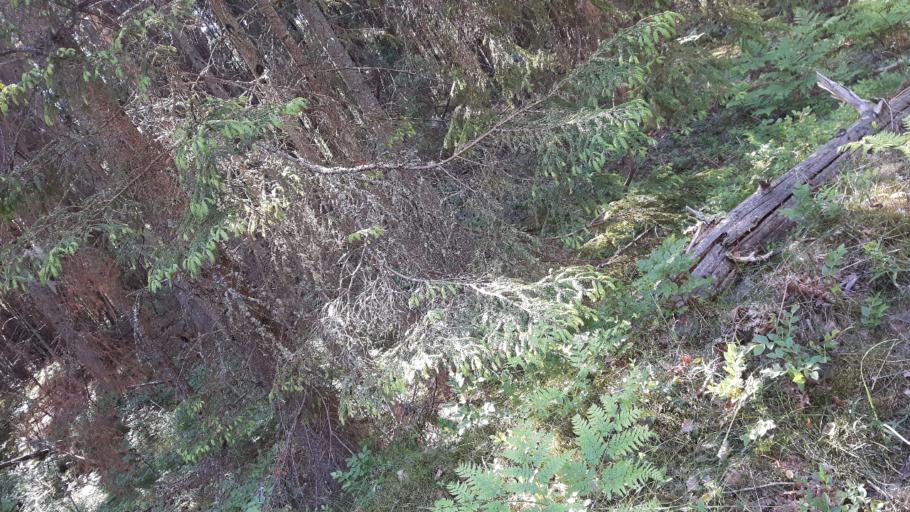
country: LV
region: Salacgrivas
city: Salacgriva
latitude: 57.7206
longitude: 24.3476
